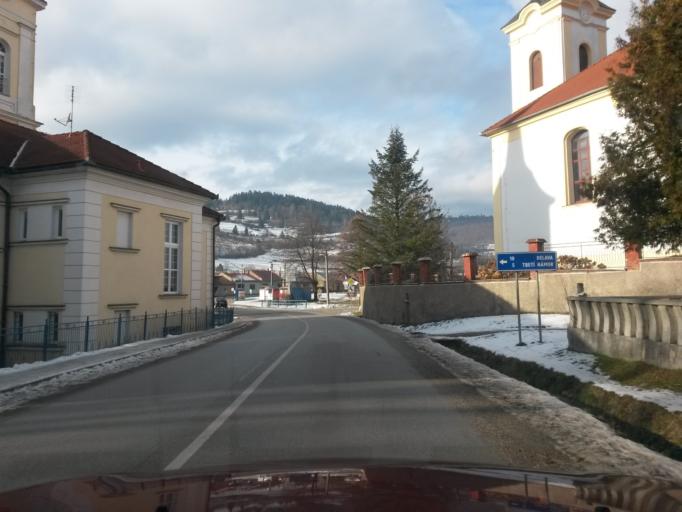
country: SK
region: Kosicky
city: Spisska Nova Ves
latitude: 48.8422
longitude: 20.6197
